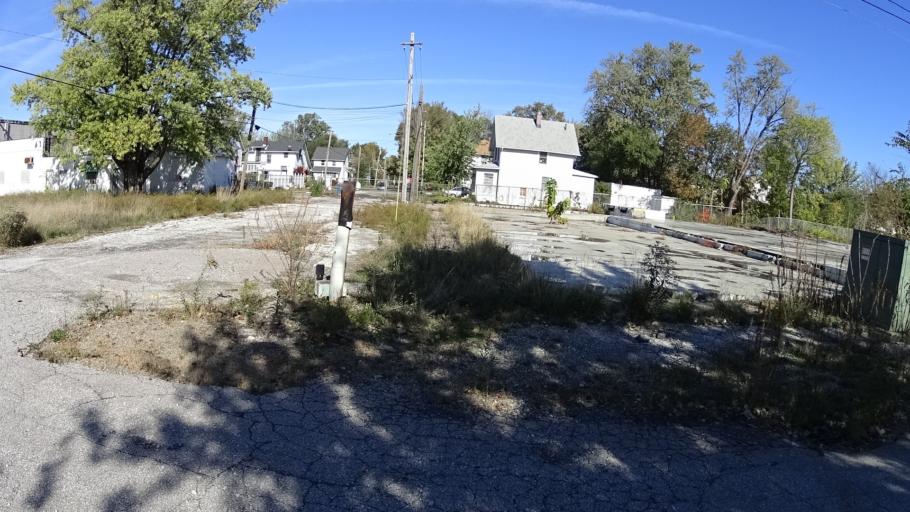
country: US
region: Ohio
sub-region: Lorain County
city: Lorain
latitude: 41.4571
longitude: -82.1821
